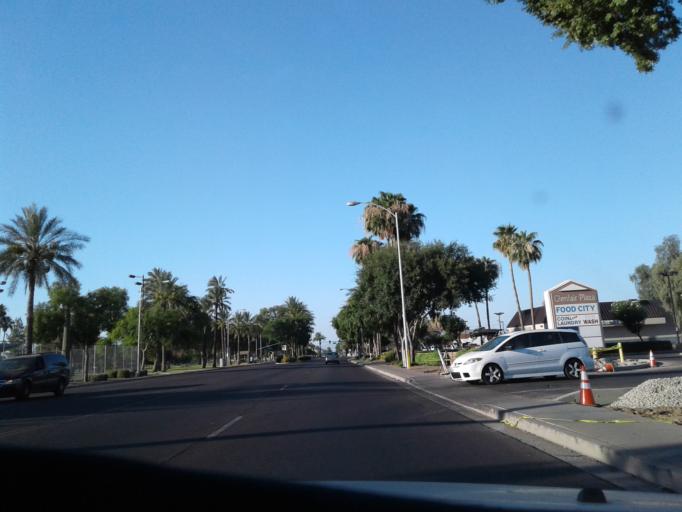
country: US
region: Arizona
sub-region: Maricopa County
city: Glendale
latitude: 33.5262
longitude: -112.1864
